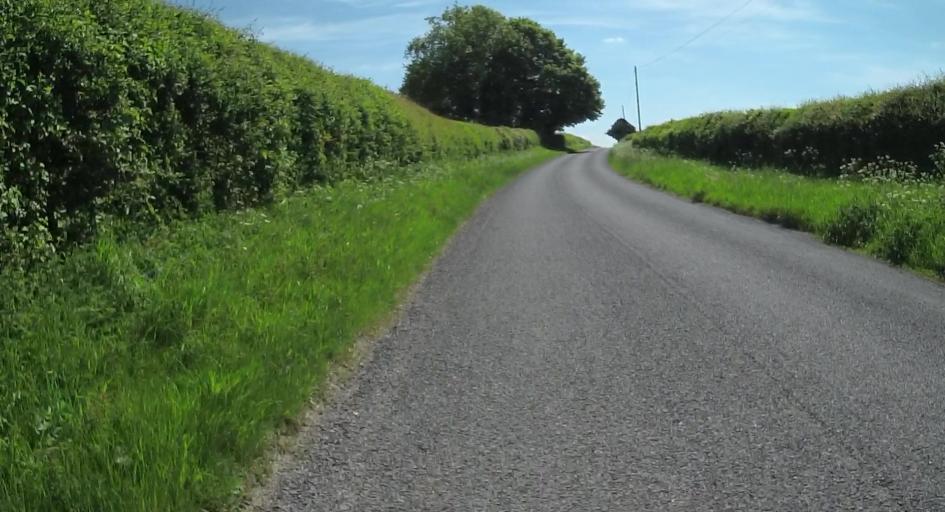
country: GB
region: England
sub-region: Hampshire
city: Four Marks
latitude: 51.1610
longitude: -1.1351
